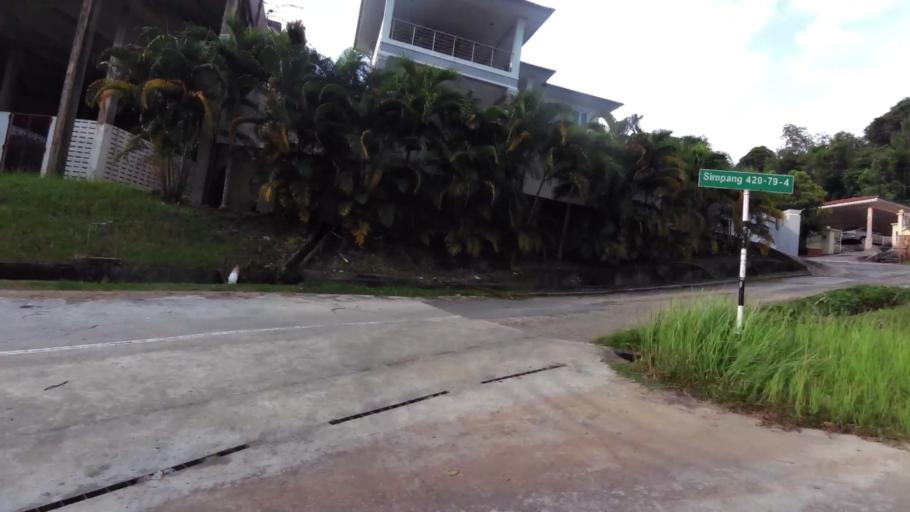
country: BN
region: Brunei and Muara
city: Bandar Seri Begawan
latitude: 4.9549
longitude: 114.9789
